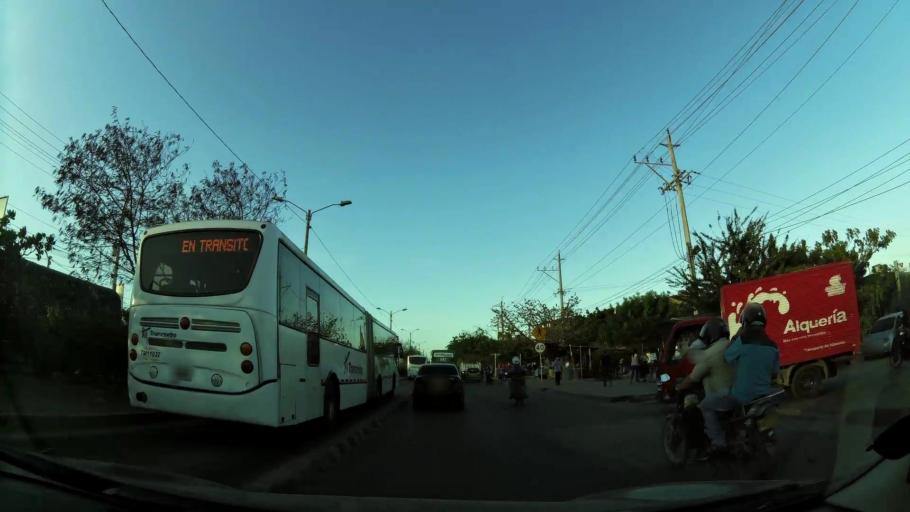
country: CO
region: Atlantico
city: Soledad
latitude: 10.9116
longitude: -74.7991
